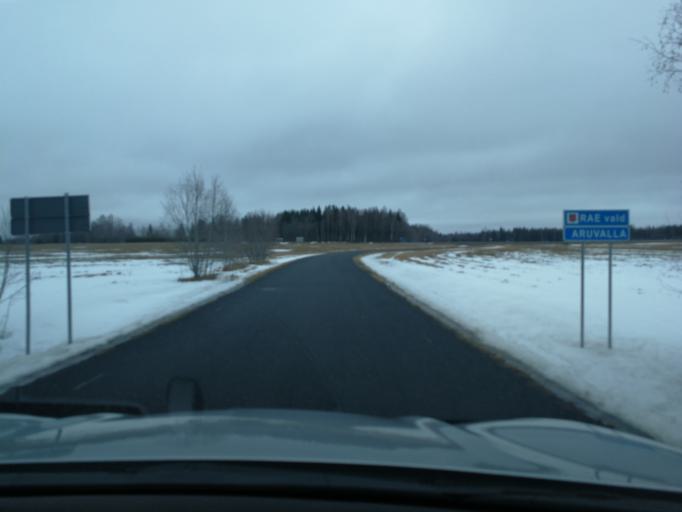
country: EE
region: Harju
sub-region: Rae vald
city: Vaida
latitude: 59.2335
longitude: 25.0199
